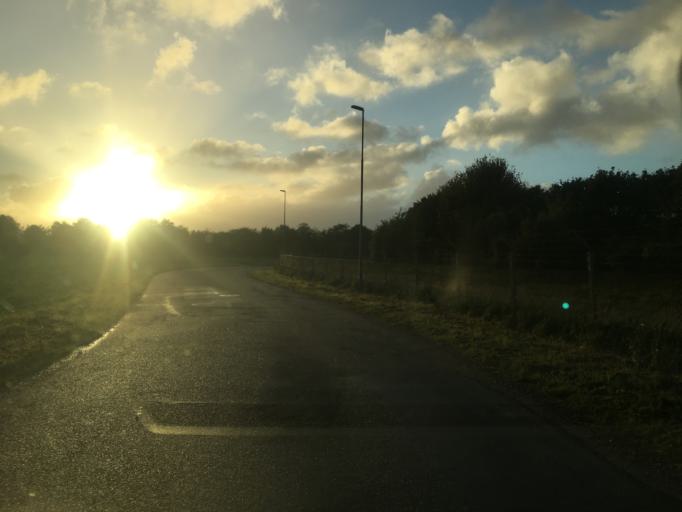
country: DK
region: South Denmark
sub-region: Tonder Kommune
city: Tonder
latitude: 54.9231
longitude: 8.8528
